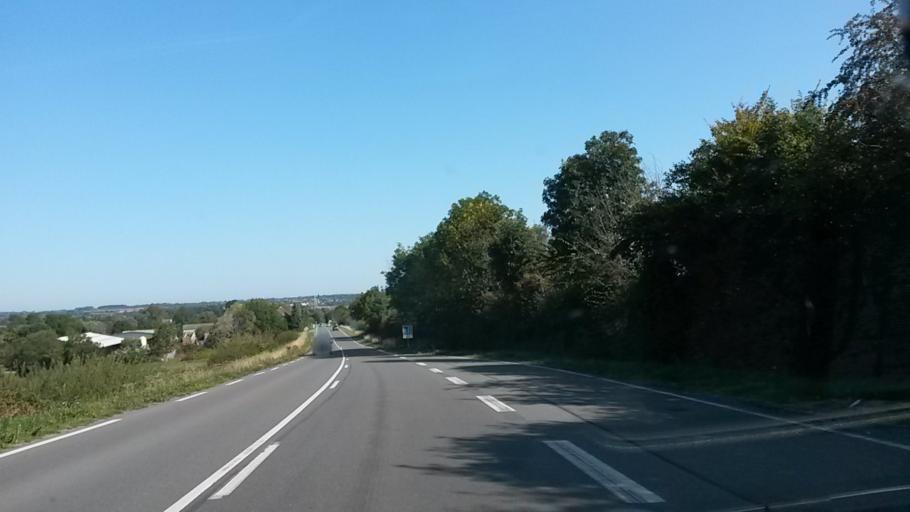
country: FR
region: Picardie
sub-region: Departement de l'Aisne
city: La Flamengrie
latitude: 50.0425
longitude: 3.9267
